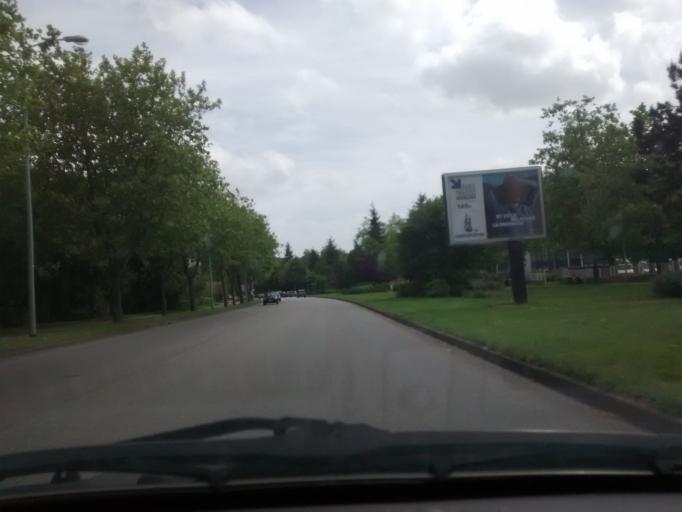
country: FR
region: Brittany
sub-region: Departement du Morbihan
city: Vannes
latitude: 47.6493
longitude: -2.7826
